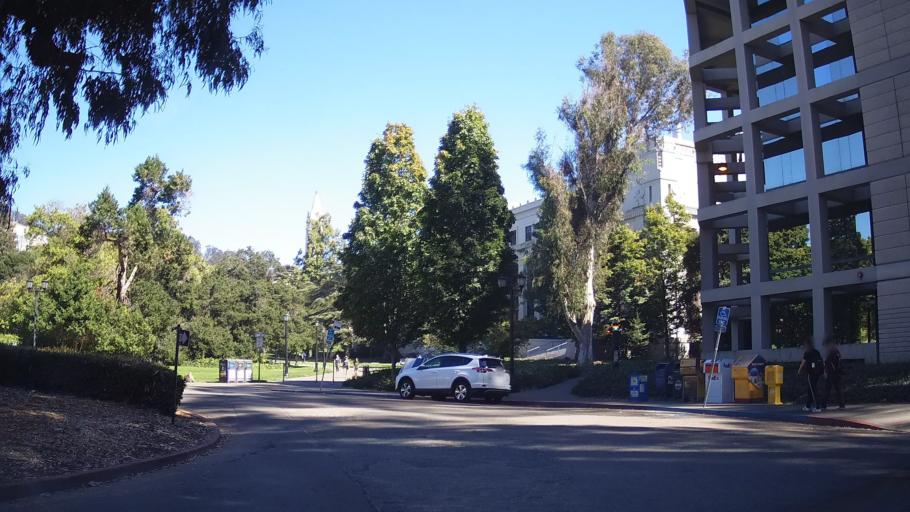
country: US
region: California
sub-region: Alameda County
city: Berkeley
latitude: 37.8719
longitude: -122.2638
